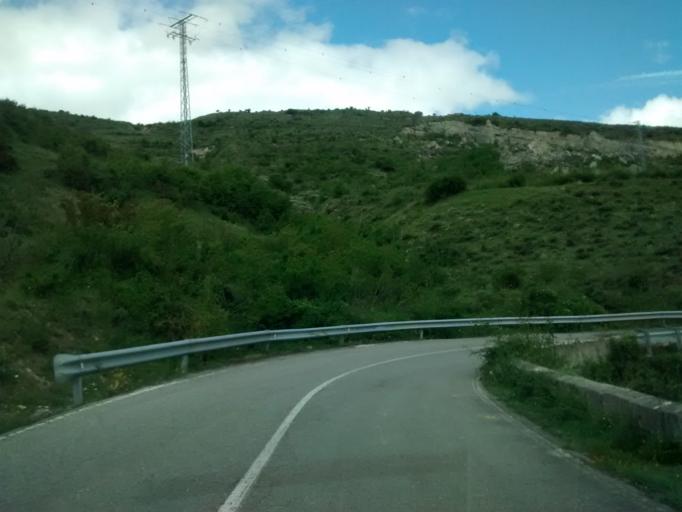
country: ES
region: La Rioja
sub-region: Provincia de La Rioja
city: Soto en Cameros
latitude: 42.2746
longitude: -2.4339
